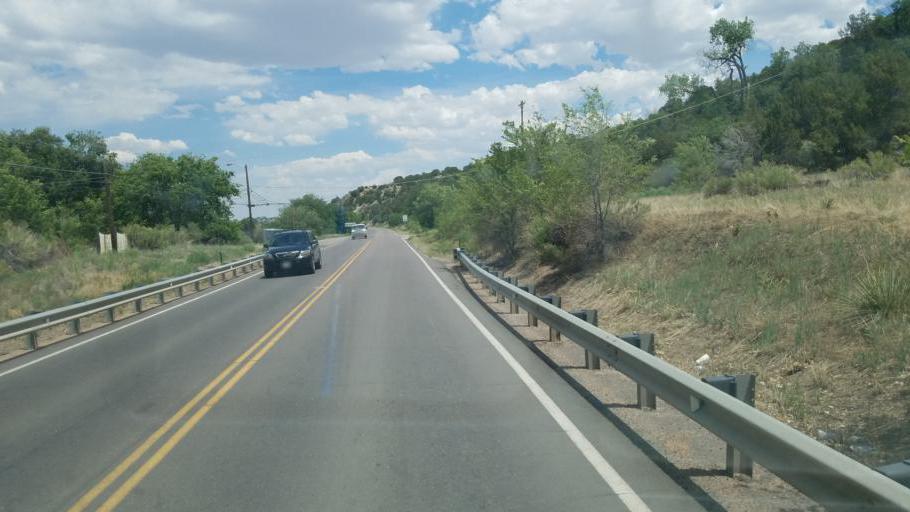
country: US
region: Colorado
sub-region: Fremont County
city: Florence
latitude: 38.4055
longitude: -105.1635
